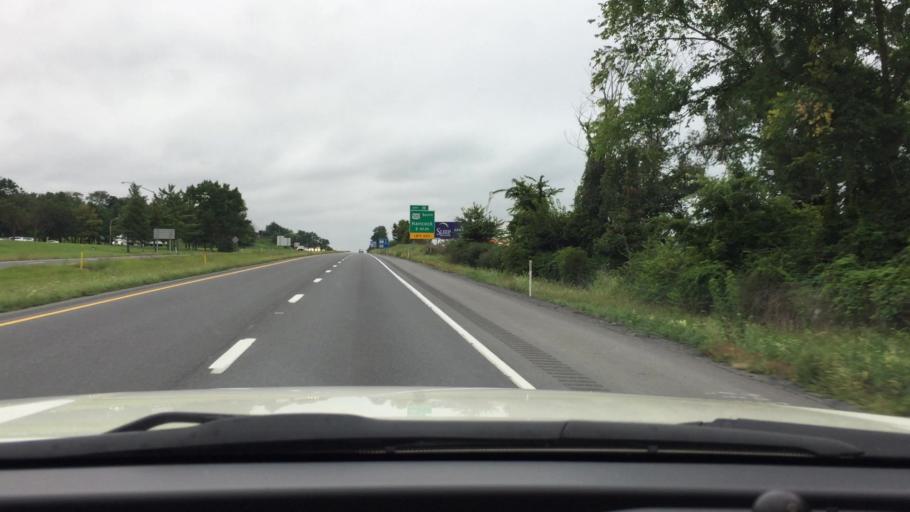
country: US
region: Maryland
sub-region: Washington County
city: Hancock
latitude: 39.7389
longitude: -78.1816
